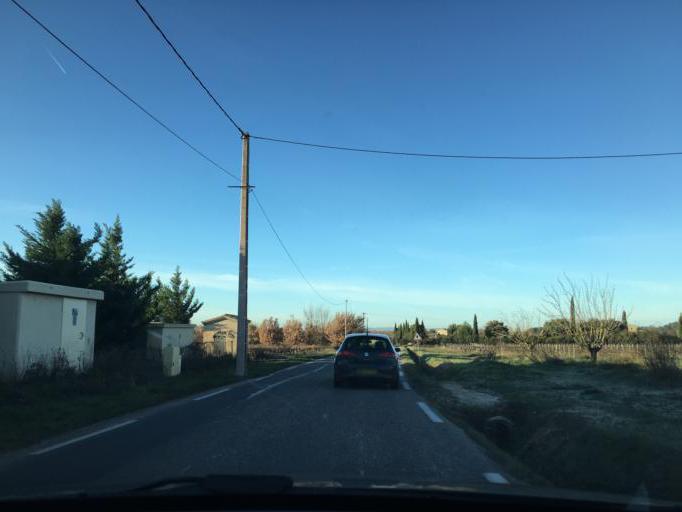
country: FR
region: Provence-Alpes-Cote d'Azur
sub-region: Departement du Vaucluse
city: Maubec
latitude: 43.8738
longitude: 5.1429
